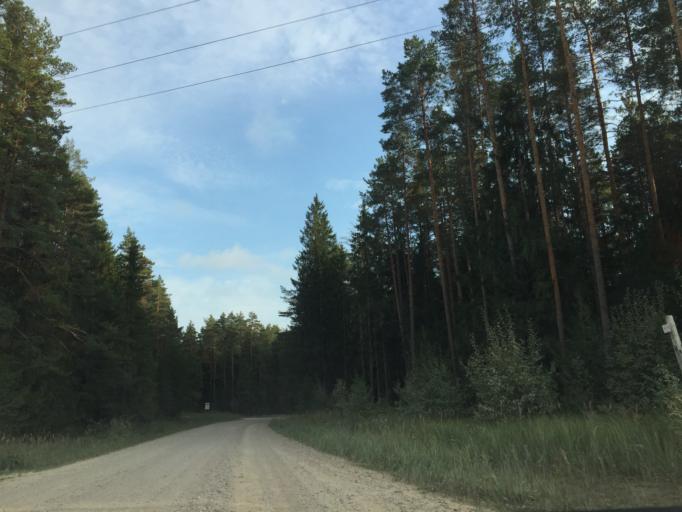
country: LV
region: Baldone
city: Baldone
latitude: 56.7897
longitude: 24.4418
